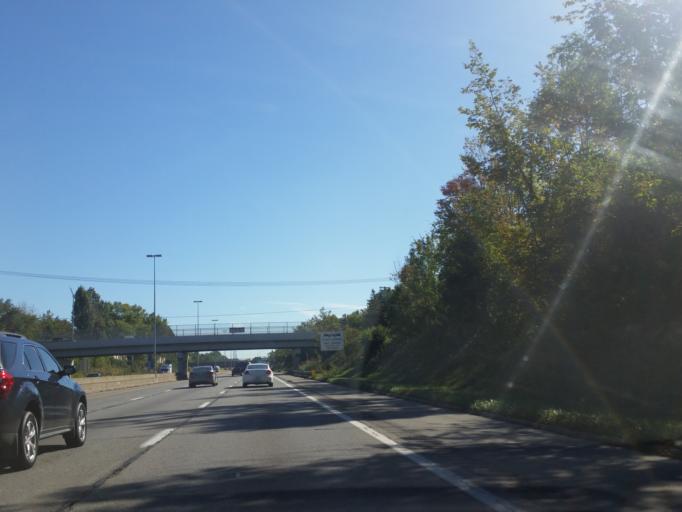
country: US
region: Ohio
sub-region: Cuyahoga County
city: Rocky River
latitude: 41.4719
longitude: -81.8489
